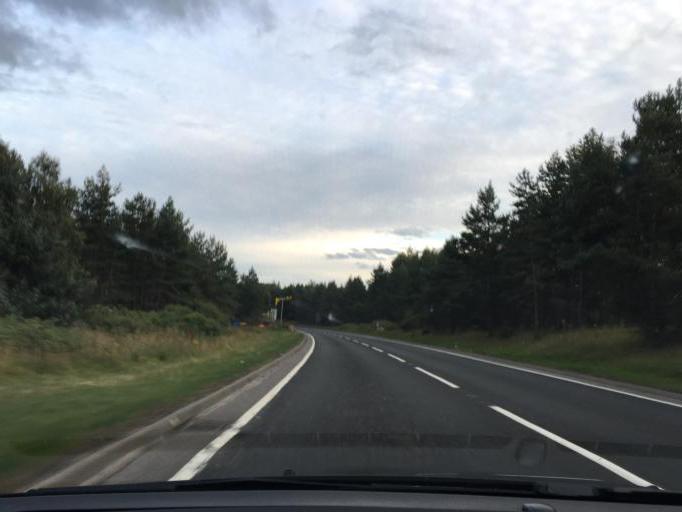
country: GB
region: Scotland
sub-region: Highland
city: Aviemore
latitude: 57.3508
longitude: -4.0064
